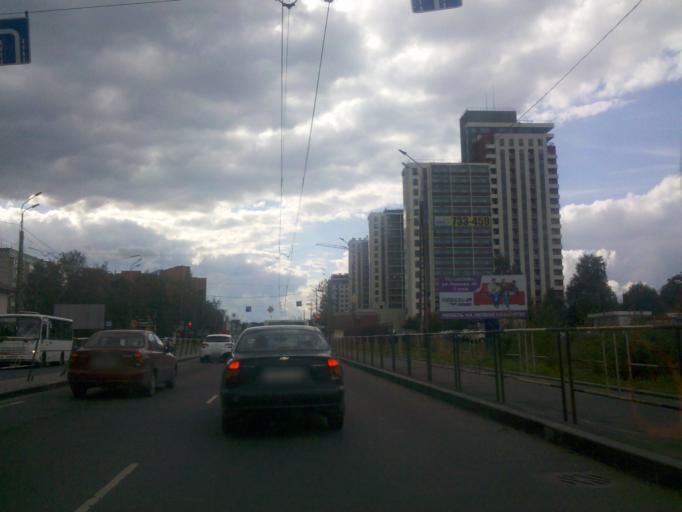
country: RU
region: Republic of Karelia
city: Petrozavodsk
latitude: 61.7850
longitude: 34.3287
